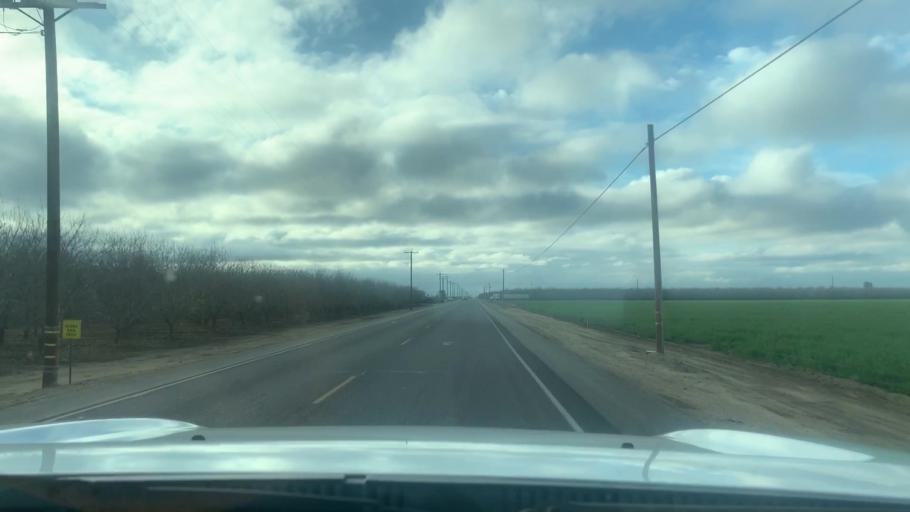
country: US
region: California
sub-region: Kern County
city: Shafter
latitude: 35.5001
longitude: -119.3461
